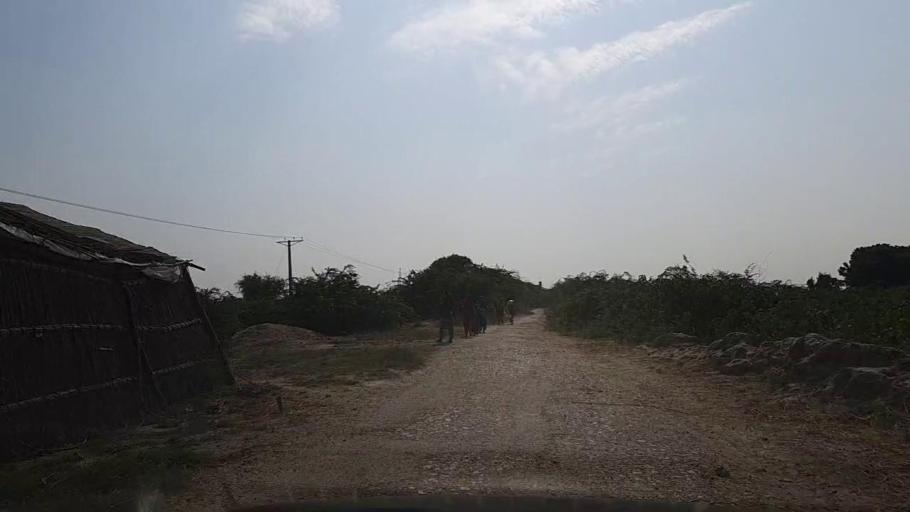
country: PK
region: Sindh
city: Thatta
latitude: 24.7538
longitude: 67.7766
